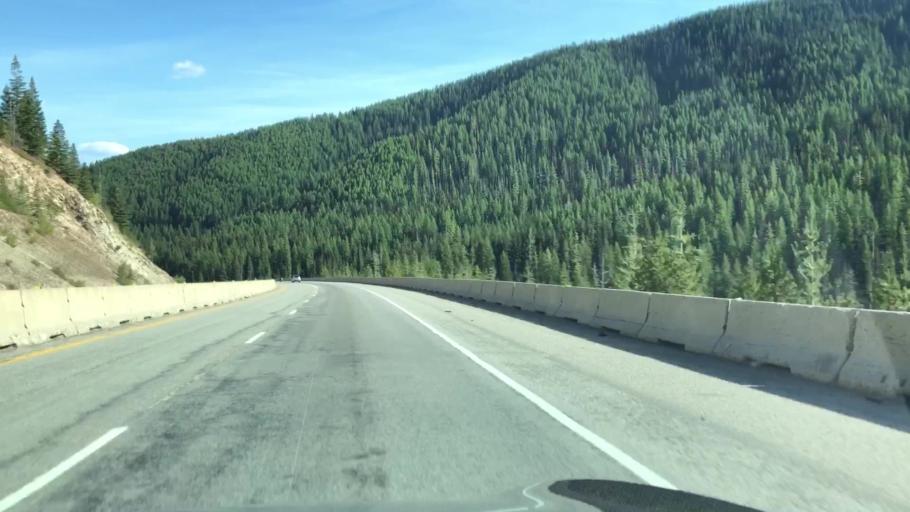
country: US
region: Idaho
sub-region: Shoshone County
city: Wallace
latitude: 47.4387
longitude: -115.6831
